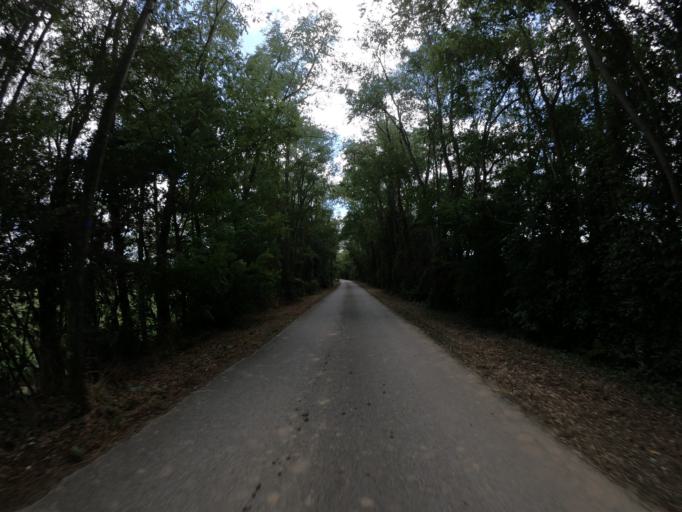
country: FR
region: Midi-Pyrenees
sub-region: Departement de l'Ariege
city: La Tour-du-Crieu
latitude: 43.1014
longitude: 1.7284
